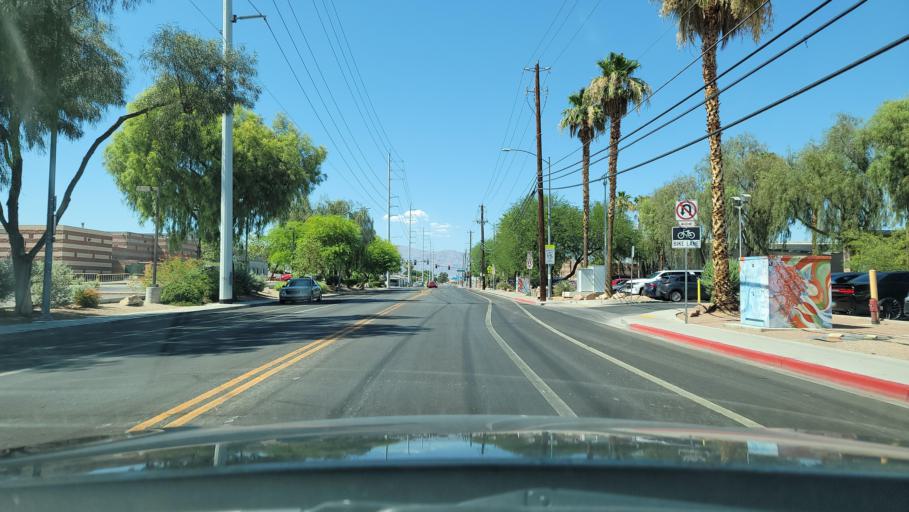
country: US
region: Nevada
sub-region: Clark County
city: Las Vegas
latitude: 36.1940
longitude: -115.1563
